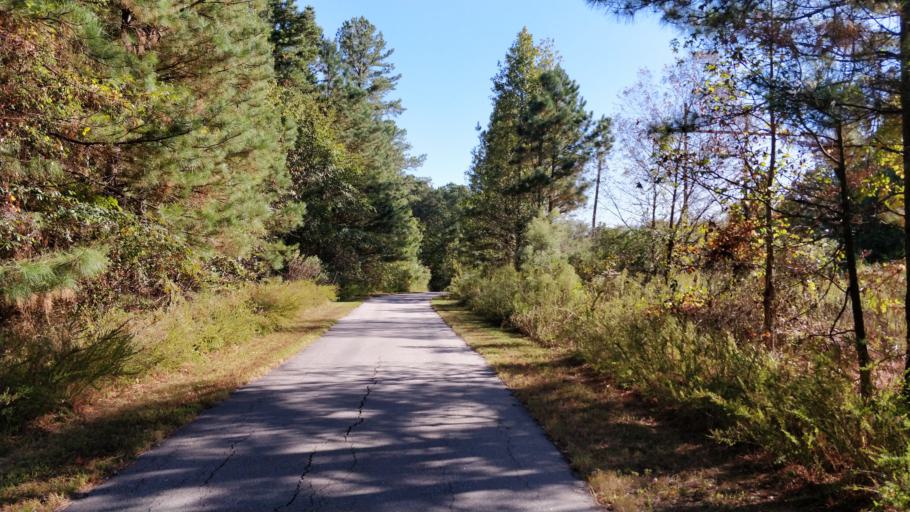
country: US
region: North Carolina
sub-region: Wake County
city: Morrisville
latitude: 35.8343
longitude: -78.8428
